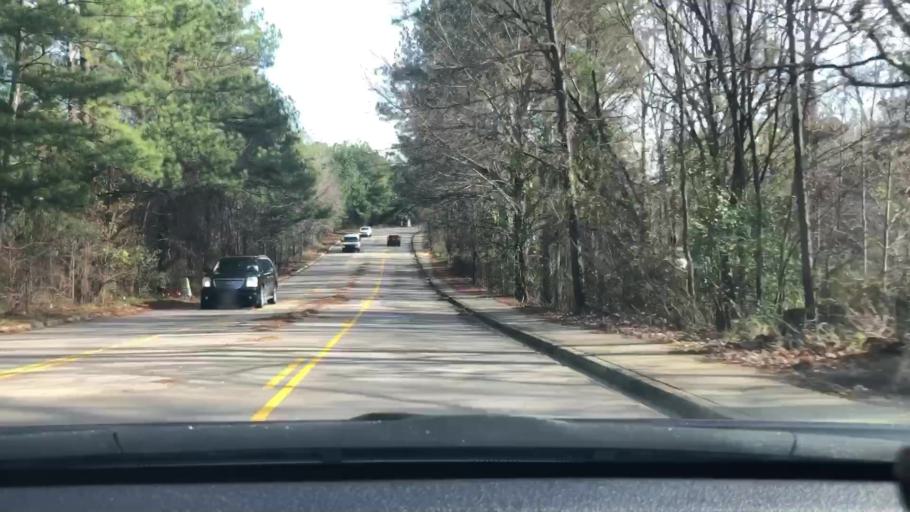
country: US
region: South Carolina
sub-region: Lexington County
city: Irmo
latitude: 34.0895
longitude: -81.1679
